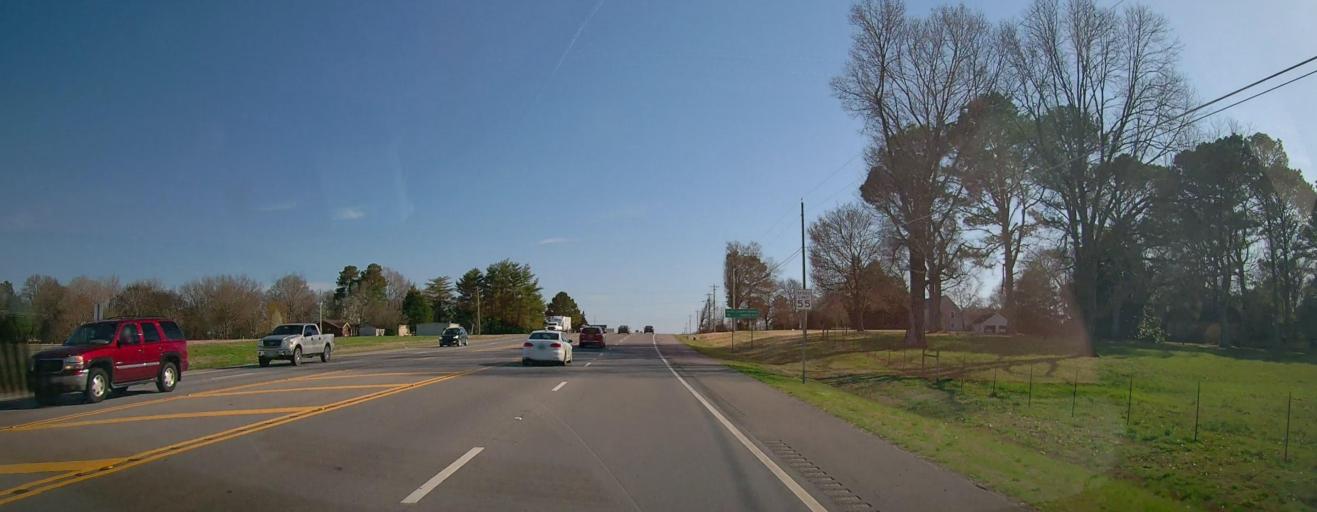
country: US
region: Alabama
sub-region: Colbert County
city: Muscle Shoals
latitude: 34.7113
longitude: -87.6349
